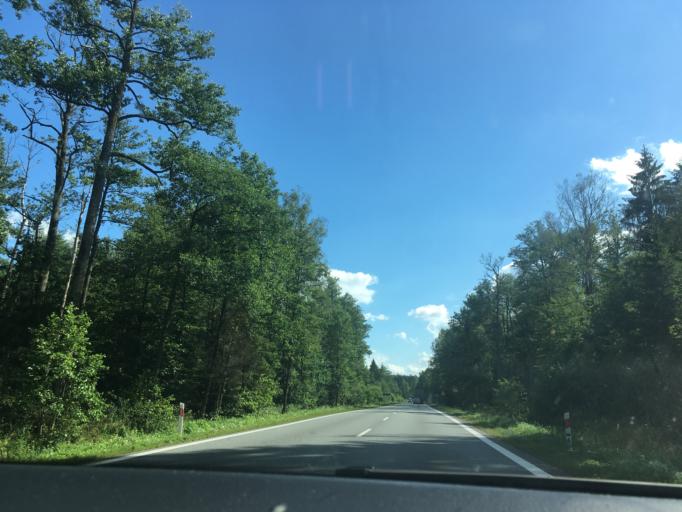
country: PL
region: Podlasie
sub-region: Powiat bialostocki
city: Wasilkow
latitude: 53.2783
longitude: 23.1208
